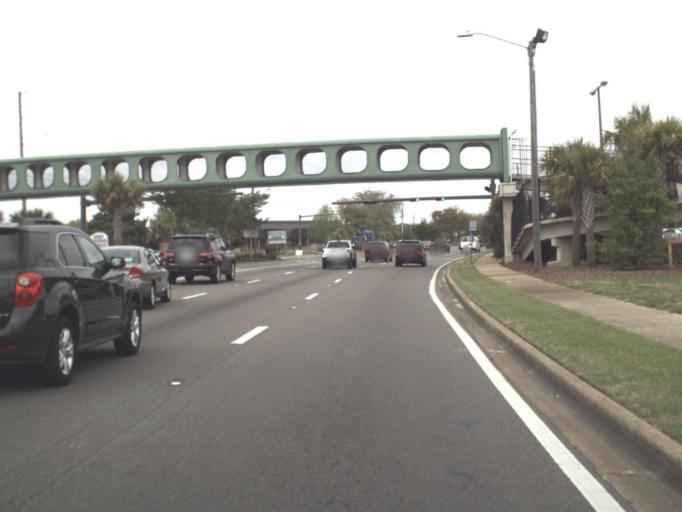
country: US
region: Florida
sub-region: Santa Rosa County
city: Gulf Breeze
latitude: 30.3600
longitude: -87.1673
